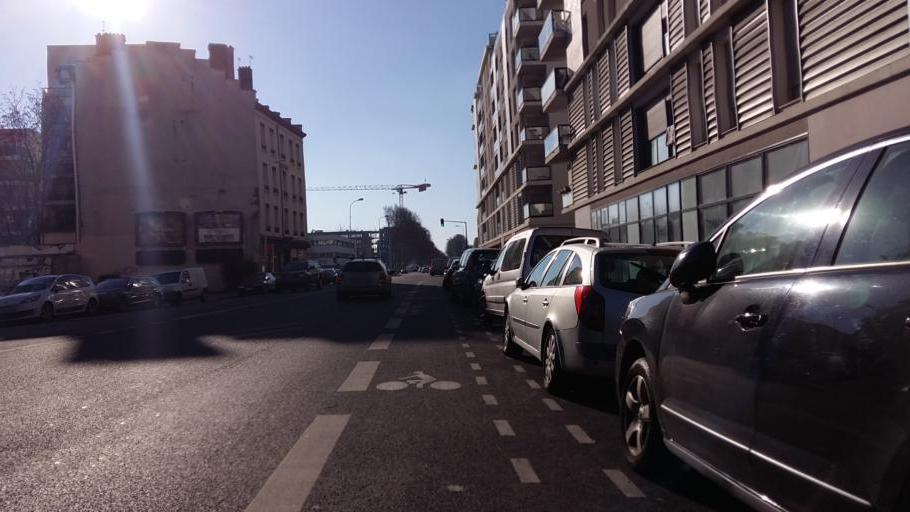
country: FR
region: Rhone-Alpes
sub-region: Departement du Rhone
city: Lyon
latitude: 45.7443
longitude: 4.8350
